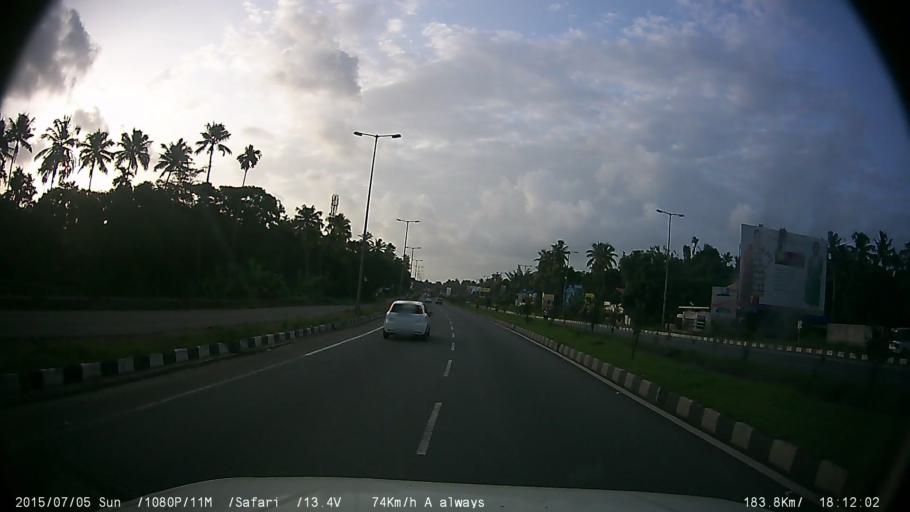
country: IN
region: Kerala
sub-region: Thrissur District
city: Kizhake Chalakudi
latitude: 10.3623
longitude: 76.3163
